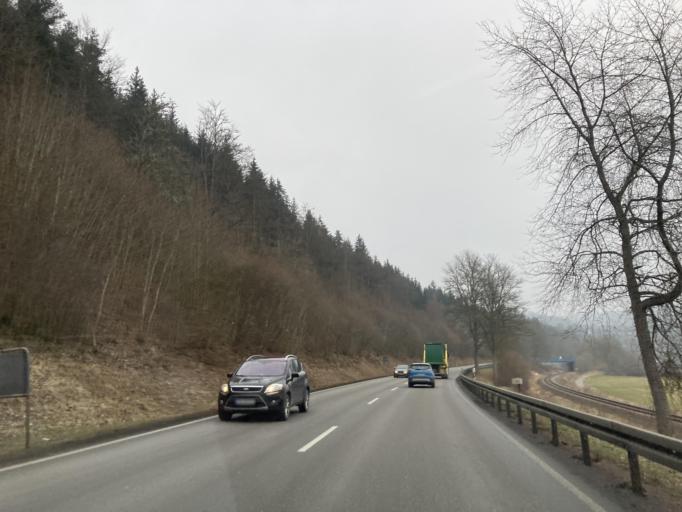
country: DE
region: Baden-Wuerttemberg
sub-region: Freiburg Region
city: Immendingen
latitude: 47.9474
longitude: 8.7561
